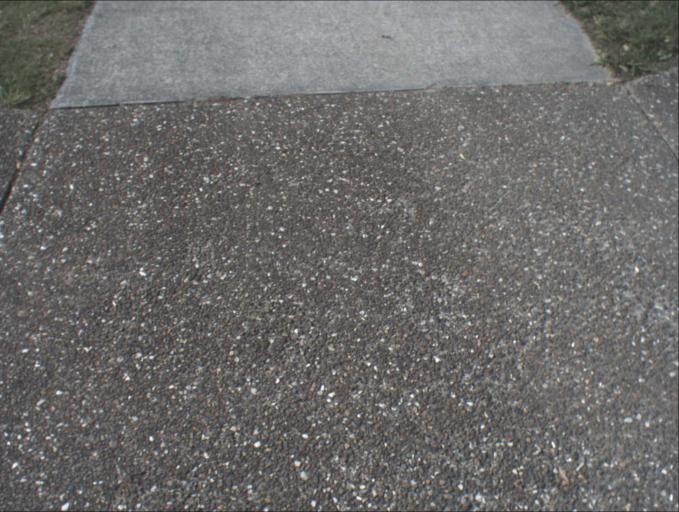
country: AU
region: Queensland
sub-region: Logan
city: Waterford West
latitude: -27.7129
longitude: 153.1543
